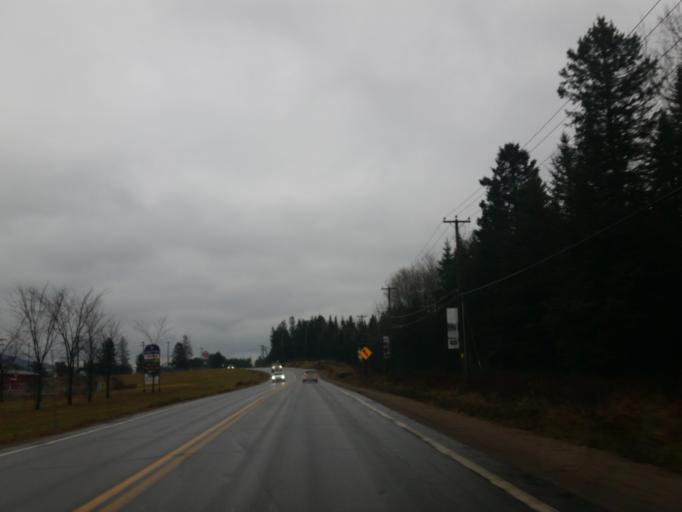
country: CA
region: Quebec
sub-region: Capitale-Nationale
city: Shannon
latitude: 46.8867
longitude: -71.5073
